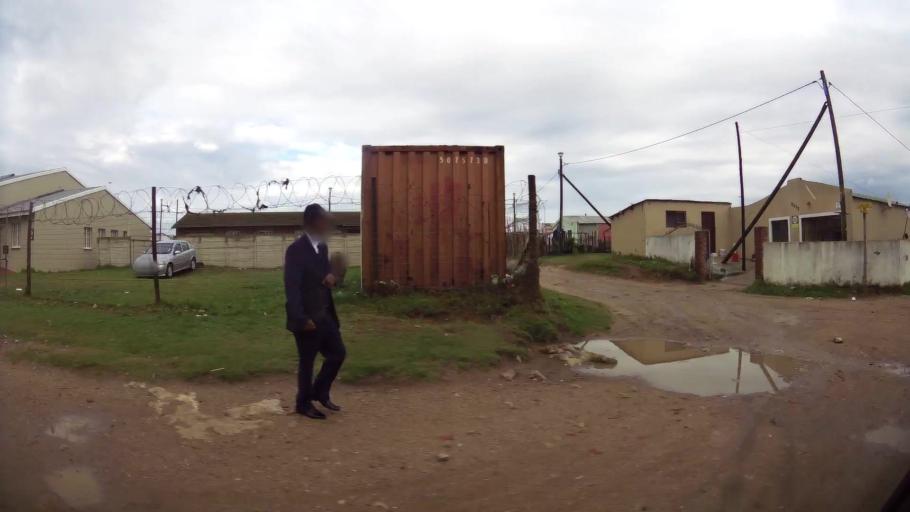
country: ZA
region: Eastern Cape
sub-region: Nelson Mandela Bay Metropolitan Municipality
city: Port Elizabeth
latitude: -33.9901
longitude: 25.5865
